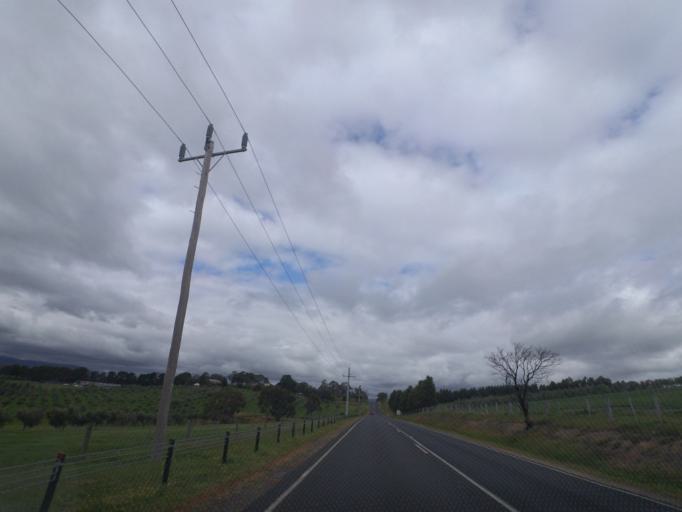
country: AU
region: Victoria
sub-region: Whittlesea
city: Whittlesea
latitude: -37.4972
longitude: 145.0950
